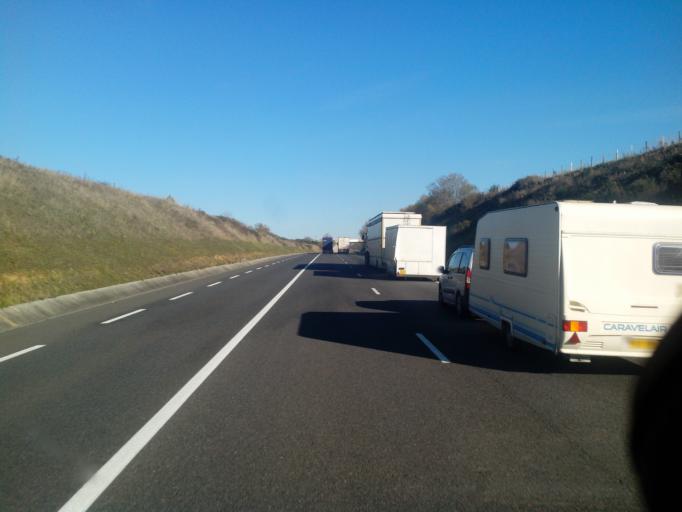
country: FR
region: Limousin
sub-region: Departement de la Haute-Vienne
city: Peyrat-de-Bellac
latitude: 46.1340
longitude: 1.0417
